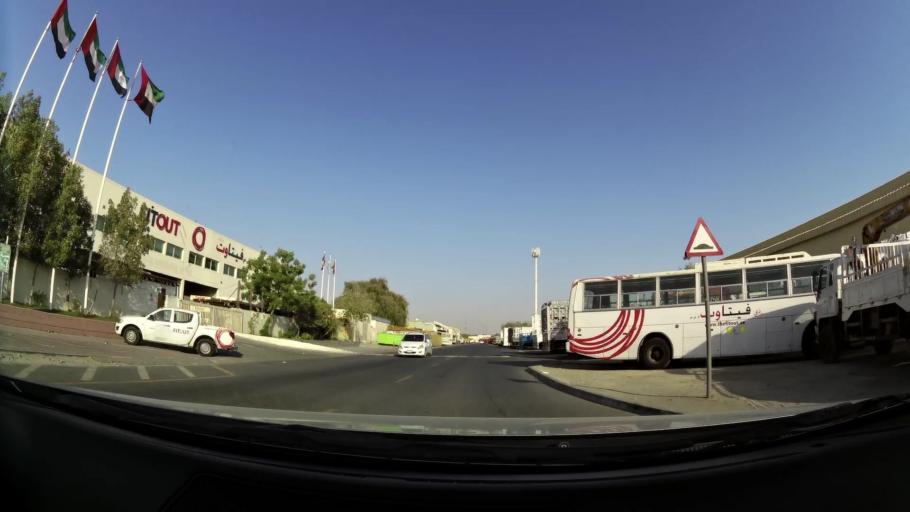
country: AE
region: Dubai
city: Dubai
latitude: 25.1320
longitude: 55.2427
